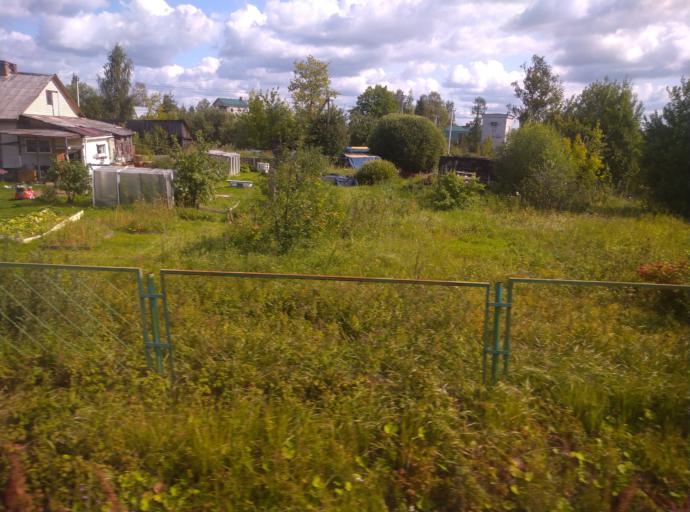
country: RU
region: Leningrad
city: Krasnyy Bor
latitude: 59.6815
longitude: 30.6996
